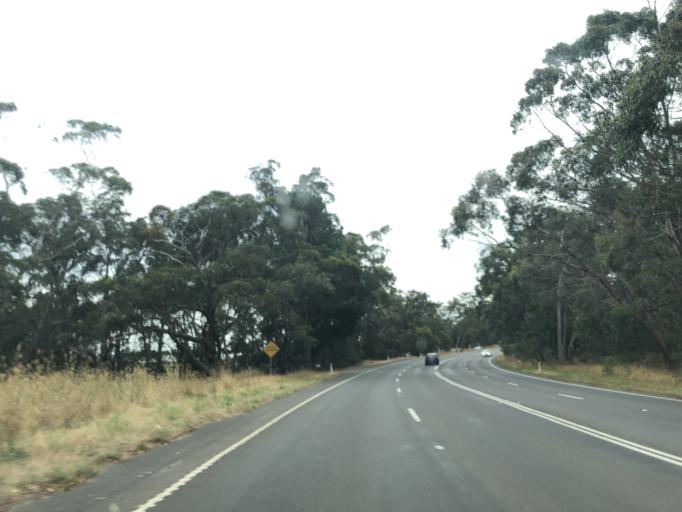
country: AU
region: Victoria
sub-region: Hume
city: Sunbury
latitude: -37.3795
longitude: 144.5276
